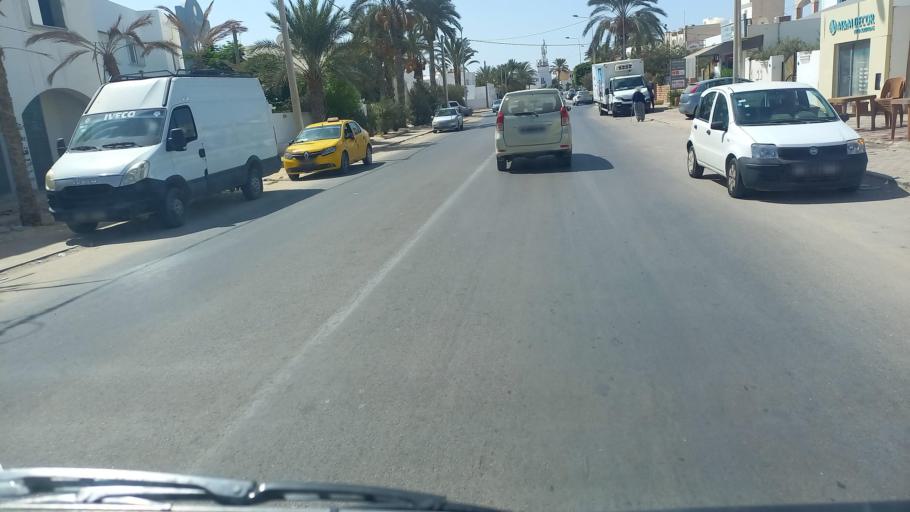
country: TN
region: Madanin
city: Houmt Souk
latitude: 33.8746
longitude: 10.8742
